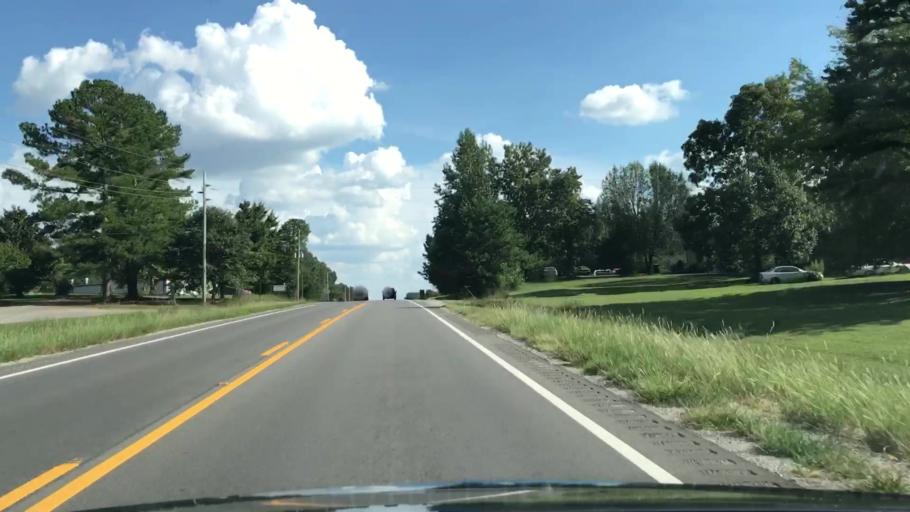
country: US
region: Alabama
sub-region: Madison County
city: Harvest
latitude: 34.9148
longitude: -86.7607
